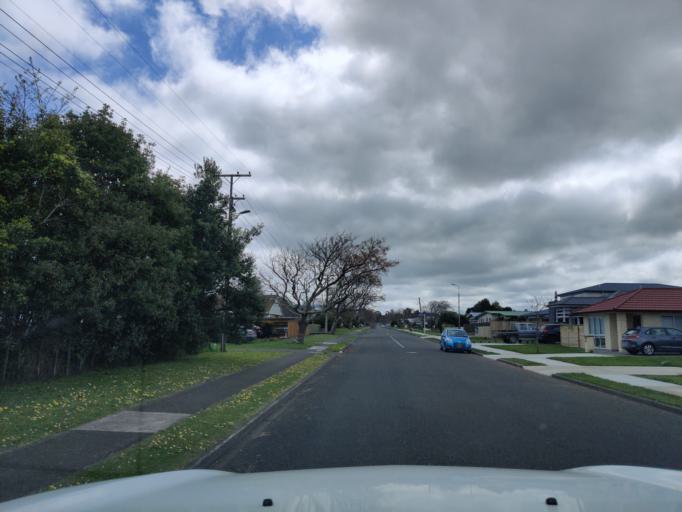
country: NZ
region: Manawatu-Wanganui
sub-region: Wanganui District
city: Wanganui
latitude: -39.9267
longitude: 175.0264
